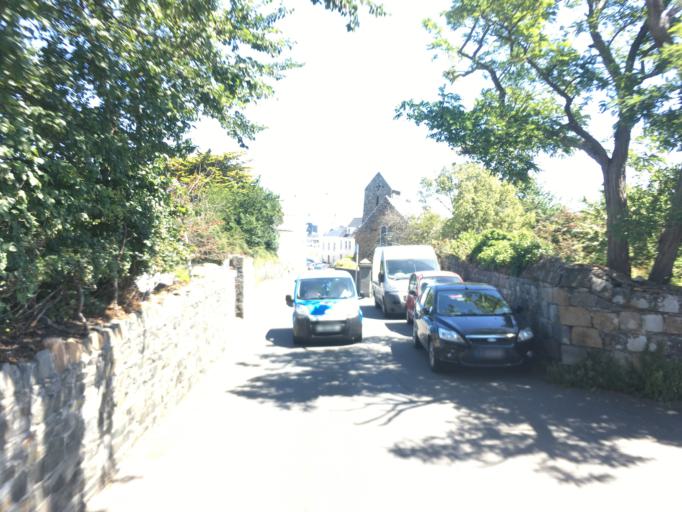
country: GG
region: St Peter Port
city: Saint Peter Port
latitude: 49.4812
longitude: -2.5174
